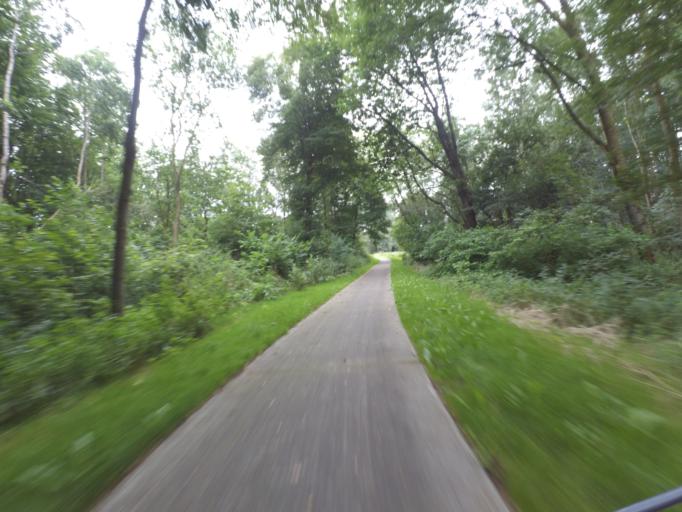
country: NL
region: Flevoland
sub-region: Gemeente Lelystad
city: Lelystad
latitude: 52.4505
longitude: 5.5484
